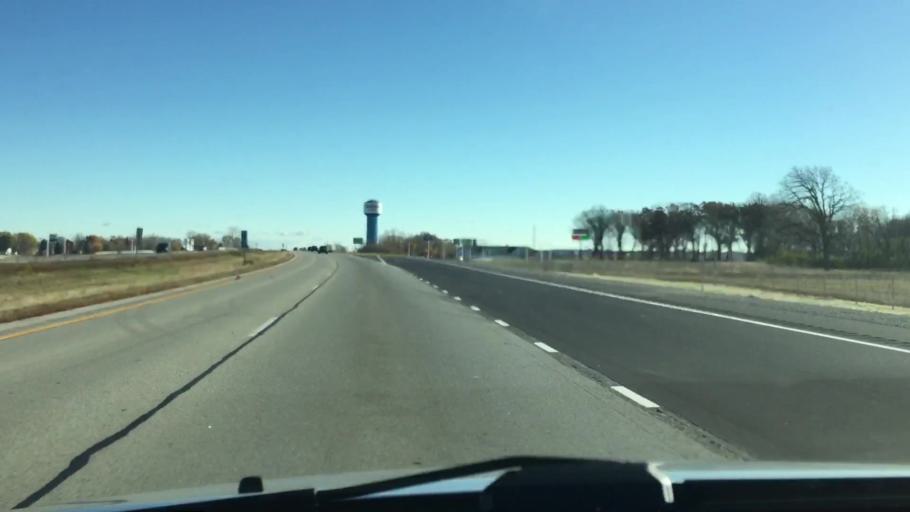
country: US
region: Wisconsin
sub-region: Outagamie County
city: Kaukauna
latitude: 44.2981
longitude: -88.2768
